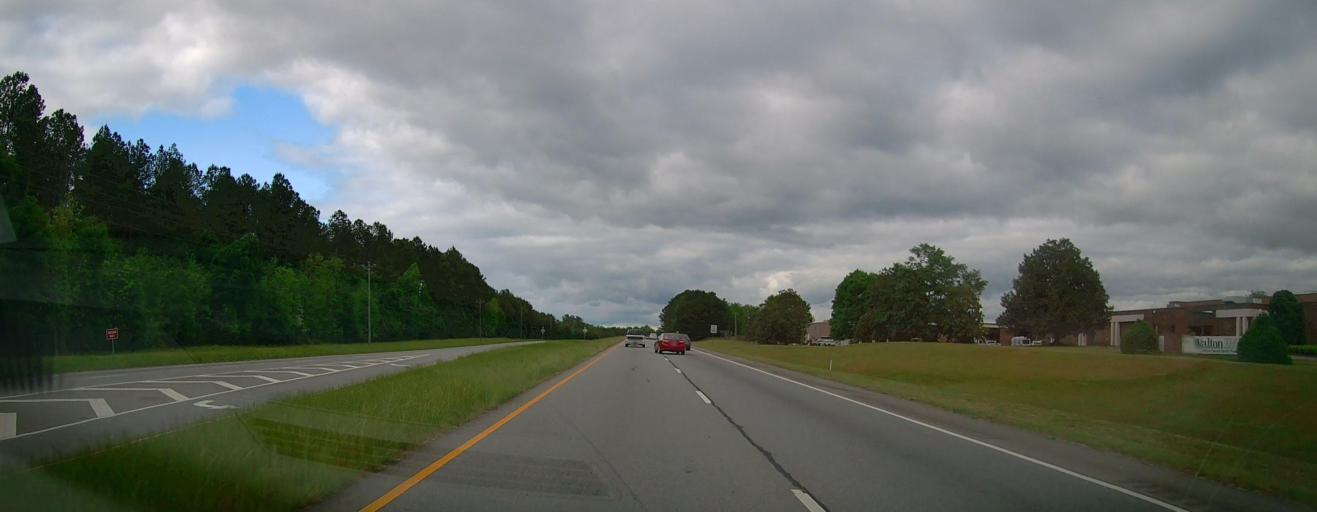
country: US
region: Georgia
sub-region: Walton County
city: Monroe
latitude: 33.8358
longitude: -83.6437
